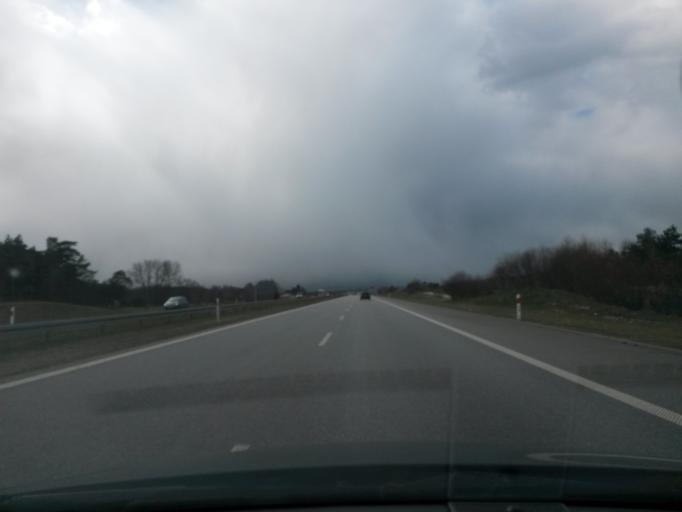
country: PL
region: Greater Poland Voivodeship
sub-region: Powiat koninski
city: Stare Miasto
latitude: 52.1605
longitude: 18.2400
